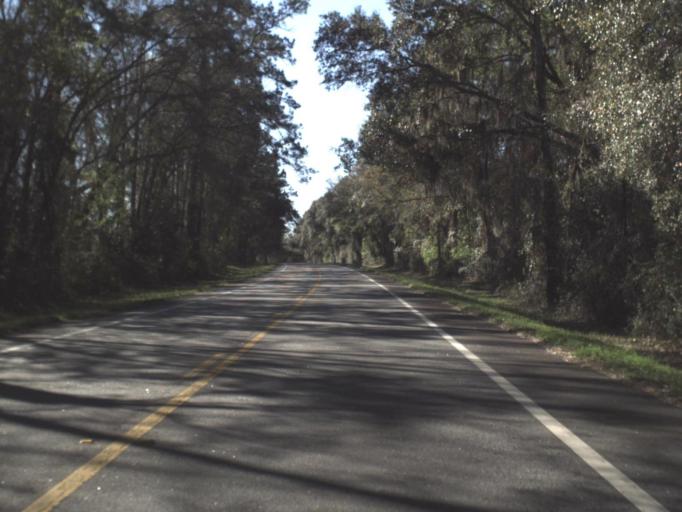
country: US
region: Georgia
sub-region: Brooks County
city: Quitman
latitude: 30.5876
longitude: -83.6395
